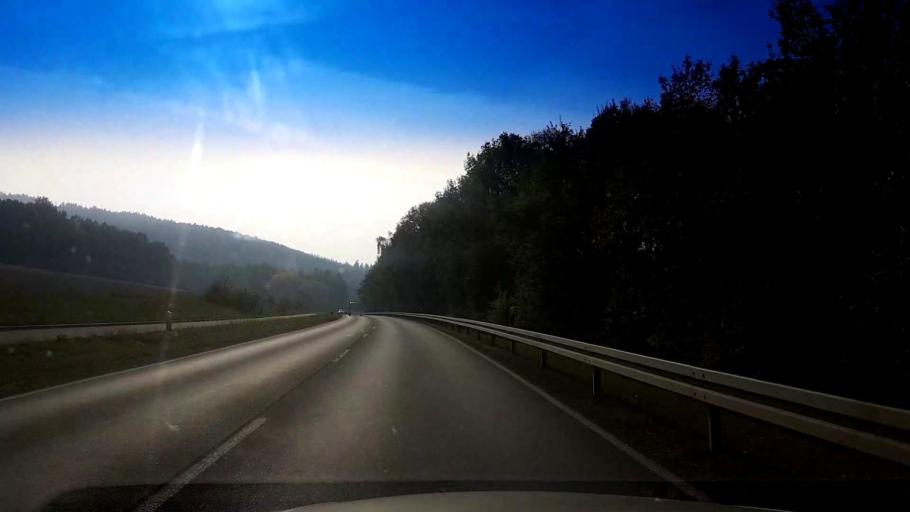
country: DE
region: Bavaria
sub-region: Upper Franconia
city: Neuenmarkt
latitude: 50.0932
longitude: 11.6073
